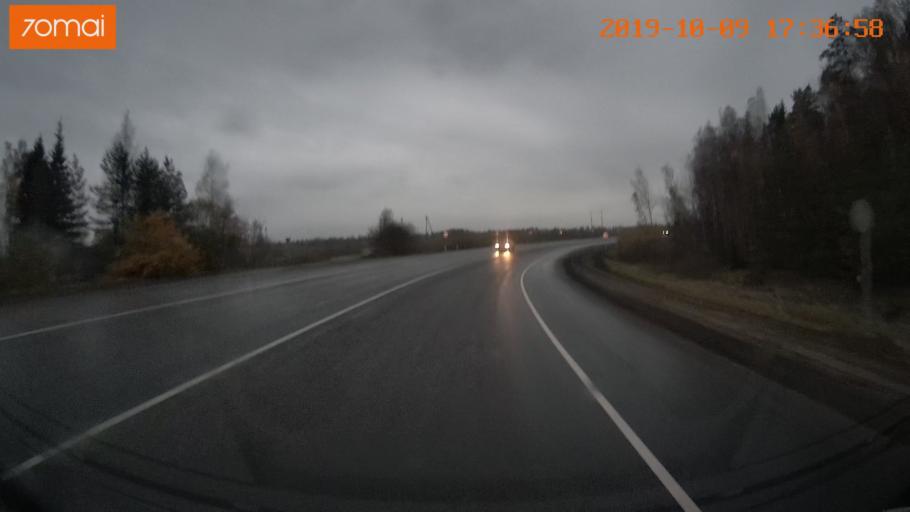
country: RU
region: Ivanovo
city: Bogorodskoye
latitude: 57.0715
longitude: 40.9905
